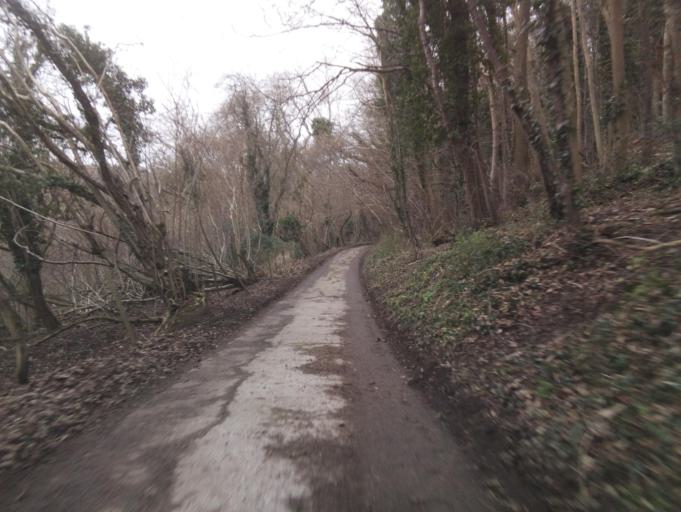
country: GB
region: England
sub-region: Wiltshire
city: Biddestone
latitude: 51.4684
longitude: -2.2339
